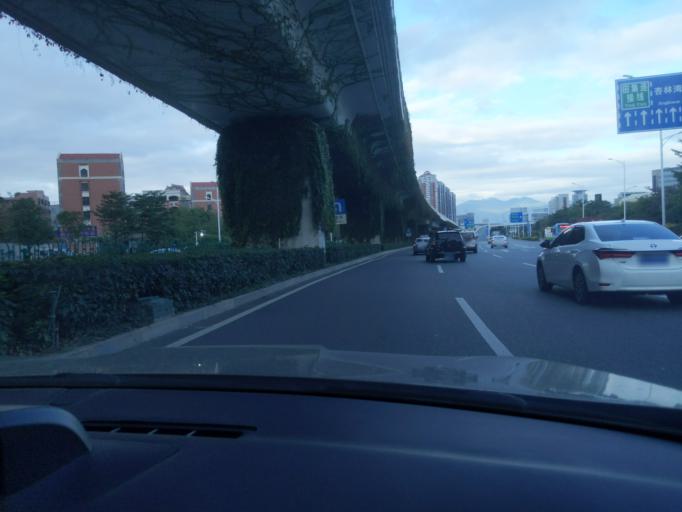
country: CN
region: Fujian
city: Yingcun
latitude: 24.5939
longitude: 118.0942
